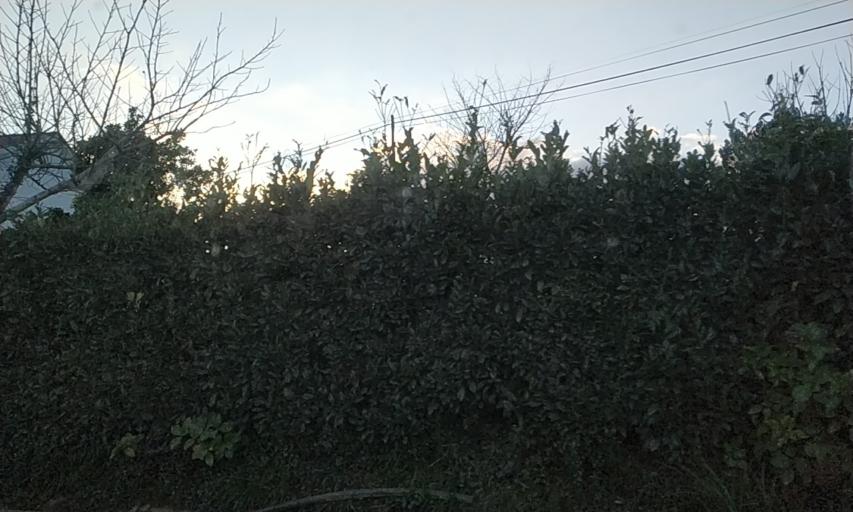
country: PT
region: Vila Real
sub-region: Mondim de Basto
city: Mondim de Basto
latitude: 41.4392
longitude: -7.9721
